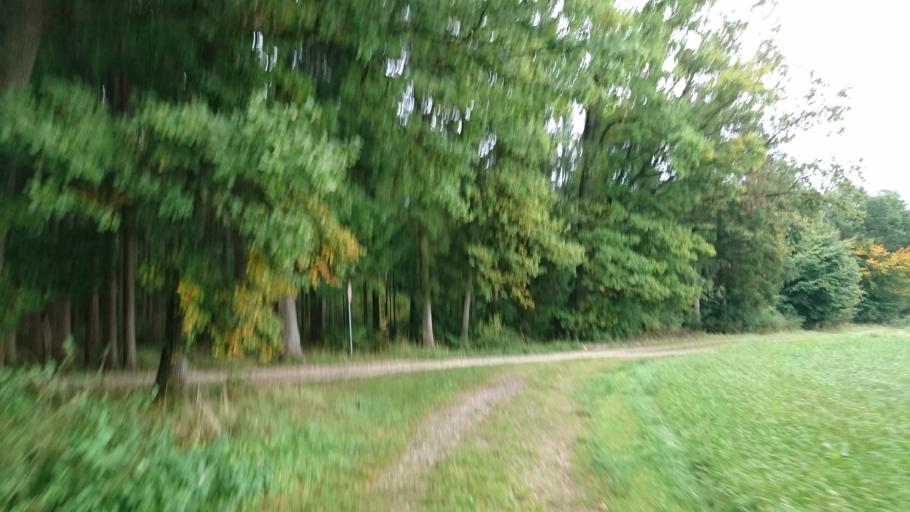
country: DE
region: Bavaria
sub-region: Swabia
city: Welden
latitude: 48.4470
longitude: 10.6474
